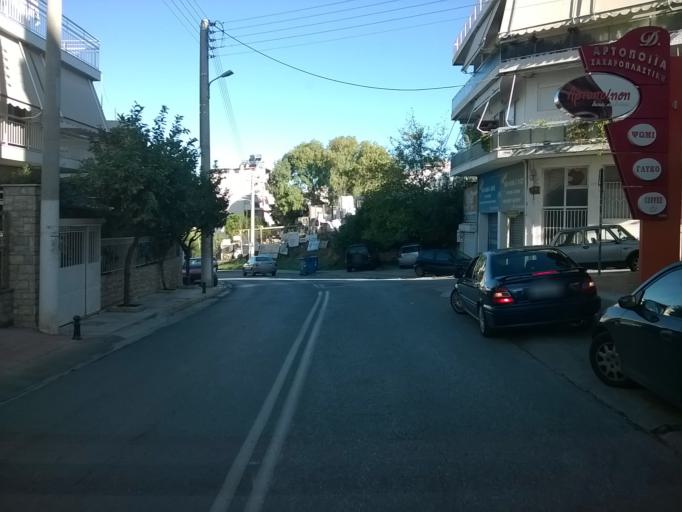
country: GR
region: Attica
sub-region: Nomarchia Athinas
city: Agios Dimitrios
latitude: 37.9314
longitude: 23.7349
